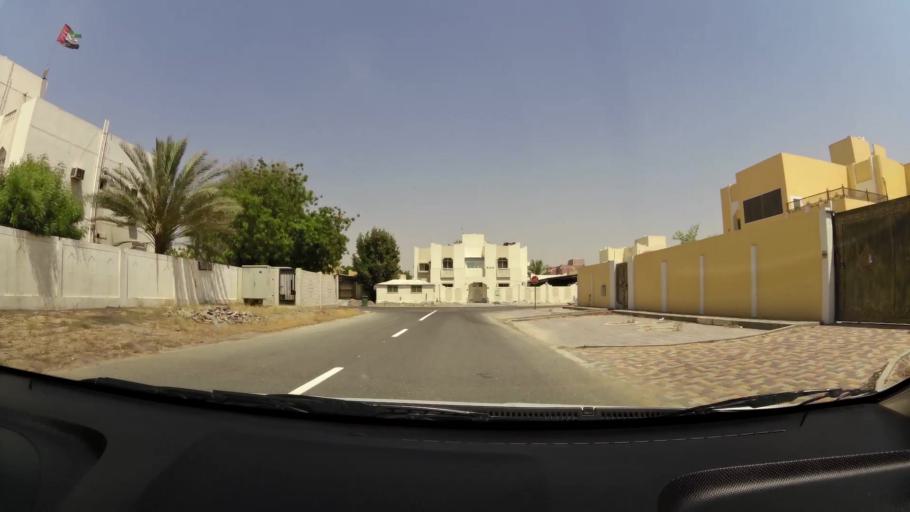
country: AE
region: Ajman
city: Ajman
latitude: 25.4274
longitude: 55.5045
